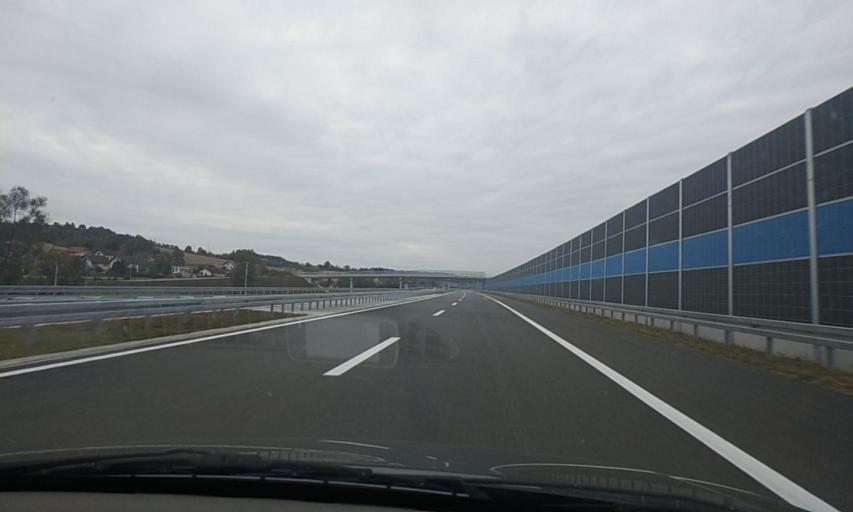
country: BA
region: Republika Srpska
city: Prnjavor
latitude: 44.8881
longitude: 17.5586
